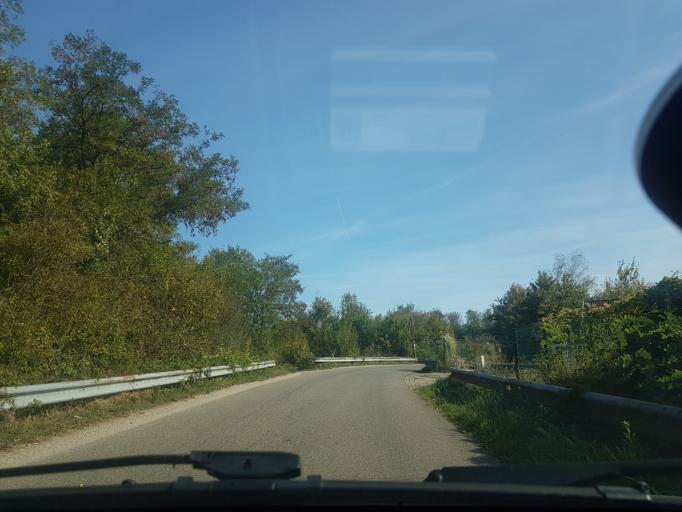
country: FR
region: Franche-Comte
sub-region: Territoire de Belfort
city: Chevremont
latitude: 47.6518
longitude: 6.9241
